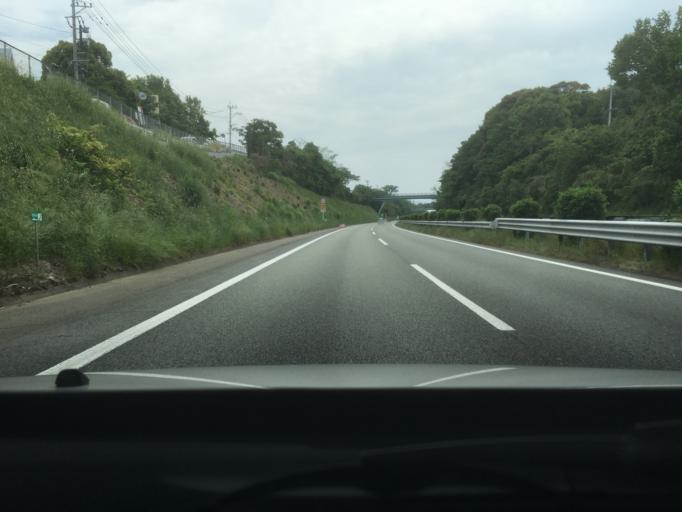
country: JP
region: Kumamoto
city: Ozu
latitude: 32.8152
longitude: 130.7920
